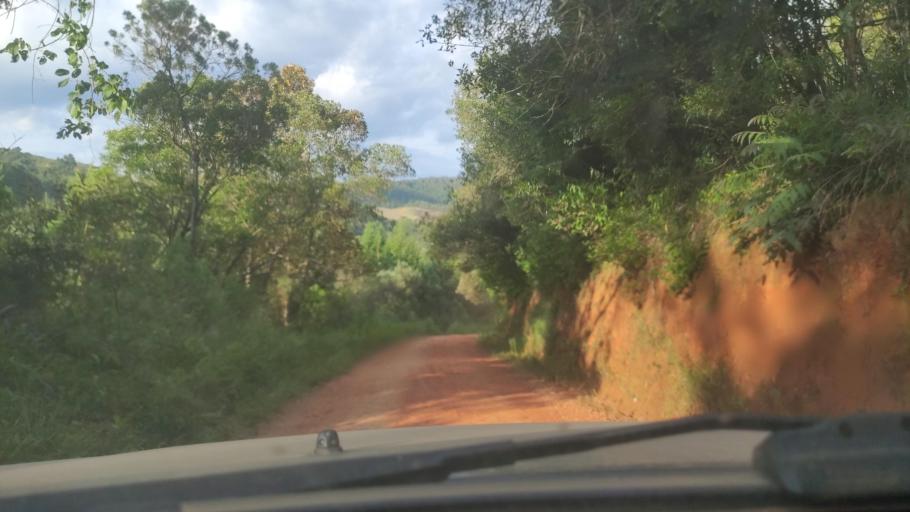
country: BR
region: Minas Gerais
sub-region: Cambui
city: Cambui
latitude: -22.7631
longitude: -45.9610
